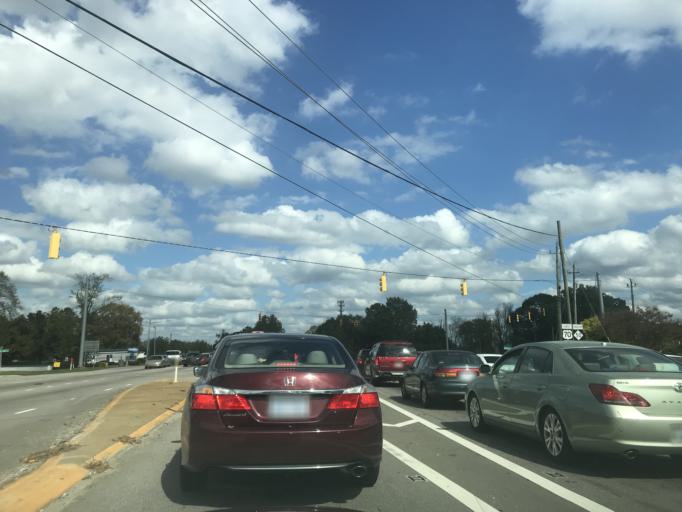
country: US
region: North Carolina
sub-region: Wake County
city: Garner
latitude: 35.7245
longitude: -78.6515
